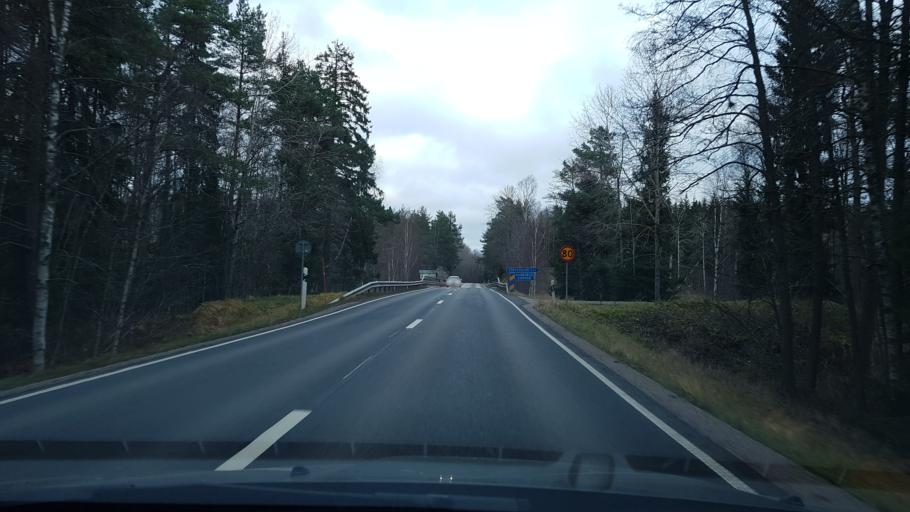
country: SE
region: Stockholm
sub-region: Norrtalje Kommun
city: Skanninge
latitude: 60.0263
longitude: 18.4139
